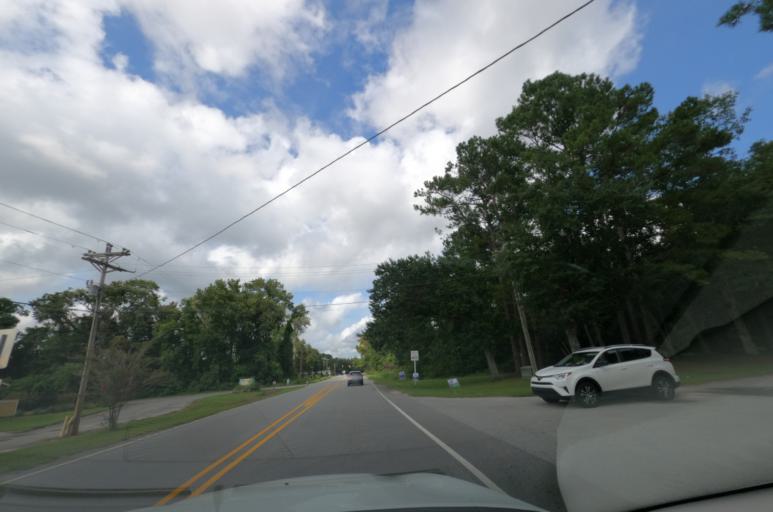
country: US
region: South Carolina
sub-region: Charleston County
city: Shell Point
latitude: 32.7194
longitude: -80.0837
